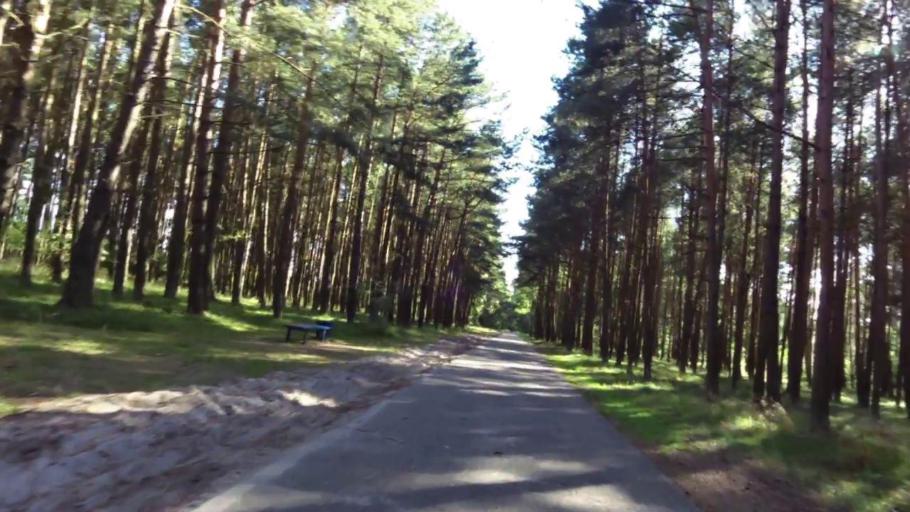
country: PL
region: West Pomeranian Voivodeship
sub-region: Powiat slawienski
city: Darlowo
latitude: 54.3712
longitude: 16.3001
